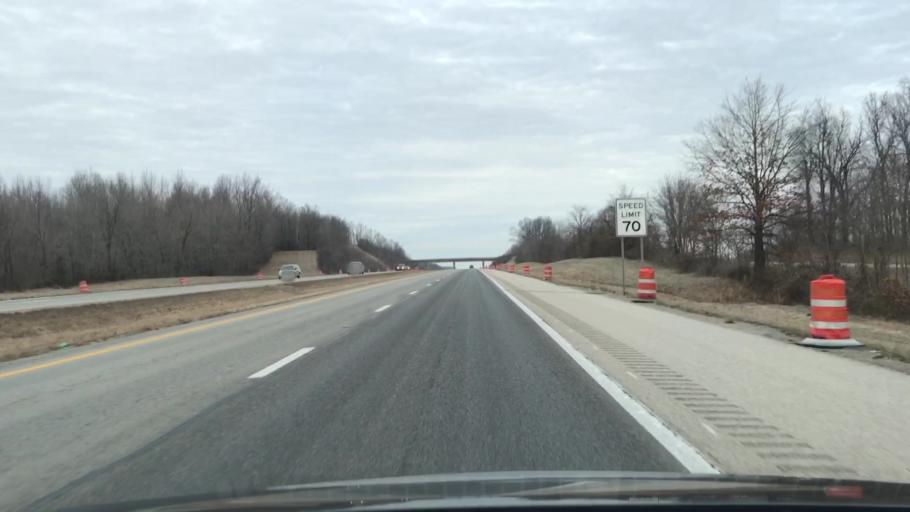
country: US
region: Kentucky
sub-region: Daviess County
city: Masonville
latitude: 37.6129
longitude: -86.9815
